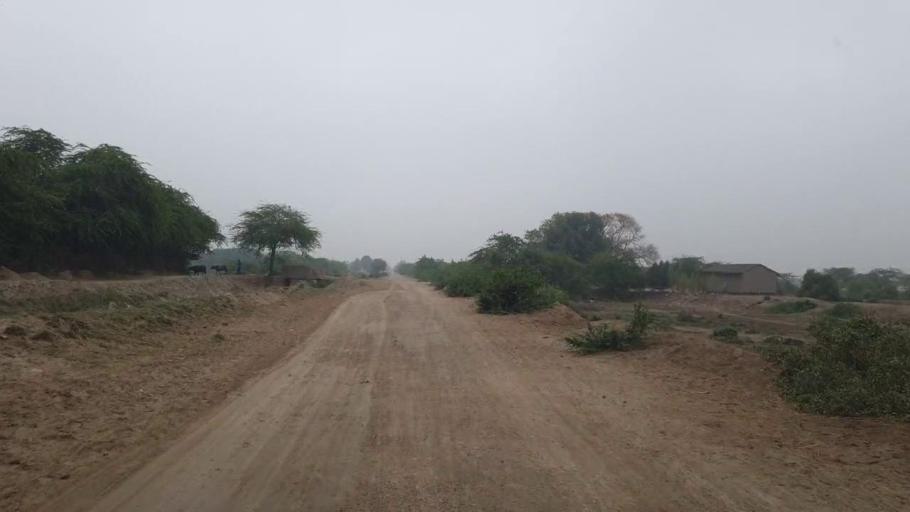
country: PK
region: Sindh
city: Badin
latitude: 24.6068
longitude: 68.6766
